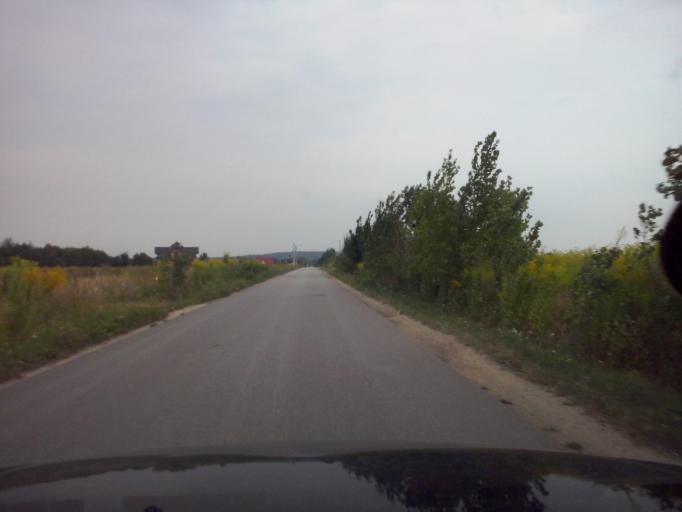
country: PL
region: Swietokrzyskie
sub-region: Powiat kielecki
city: Domaszowice
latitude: 50.8147
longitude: 20.6607
